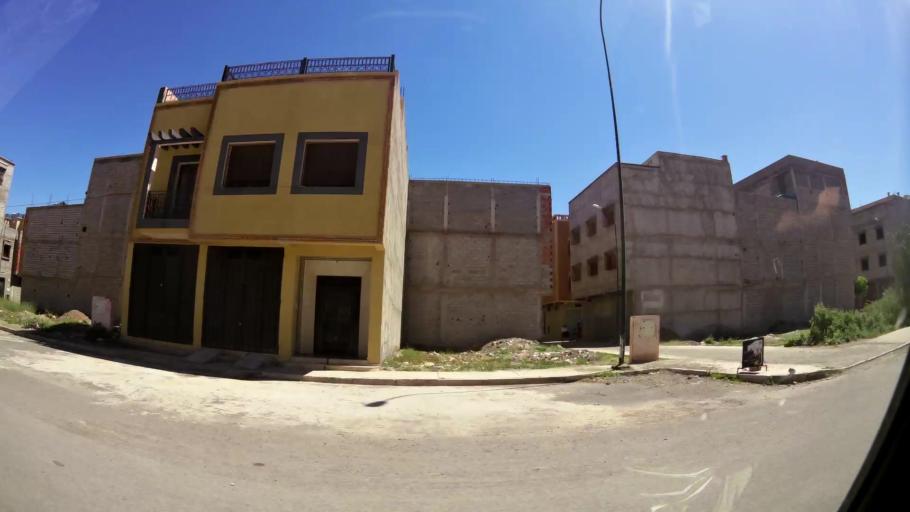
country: MA
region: Marrakech-Tensift-Al Haouz
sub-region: Marrakech
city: Marrakesh
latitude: 31.5540
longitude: -7.9793
